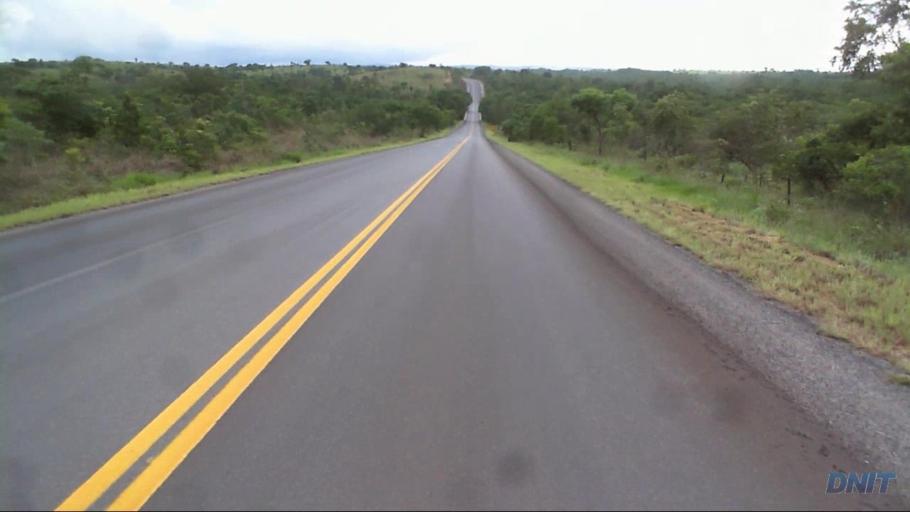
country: BR
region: Goias
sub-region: Padre Bernardo
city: Padre Bernardo
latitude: -15.2148
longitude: -48.5893
